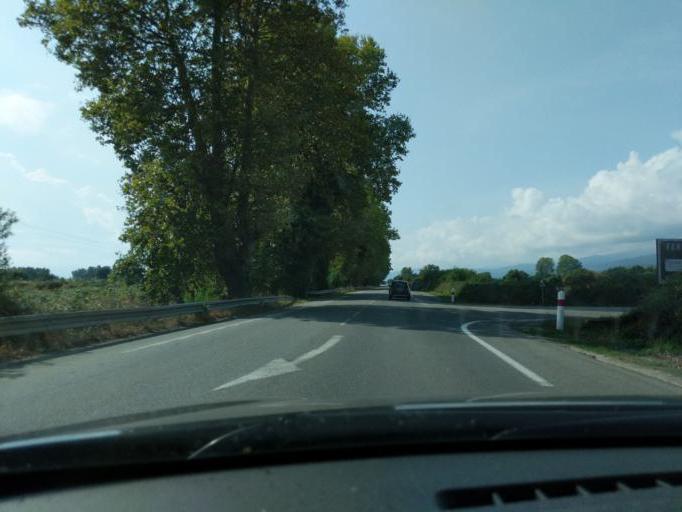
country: FR
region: Corsica
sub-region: Departement de la Haute-Corse
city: Ghisonaccia
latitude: 41.9811
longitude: 9.4002
